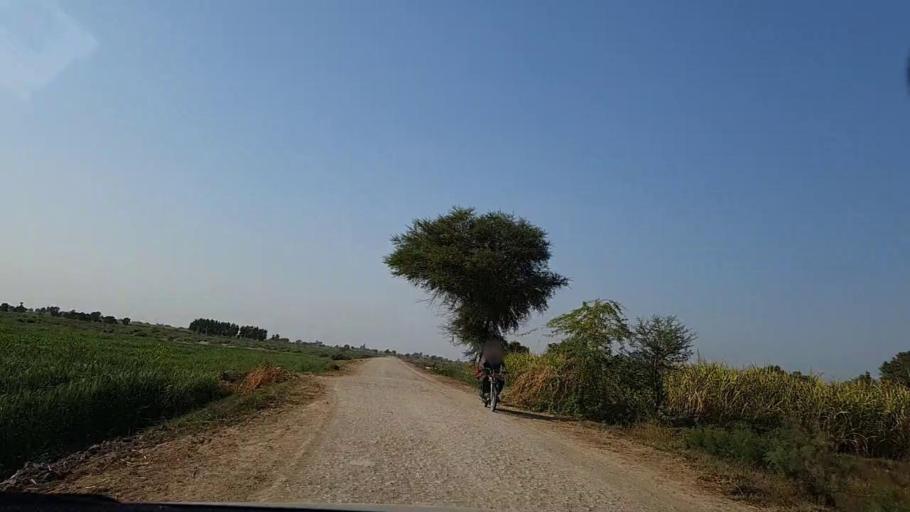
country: PK
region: Sindh
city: Digri
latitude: 25.1846
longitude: 69.0037
